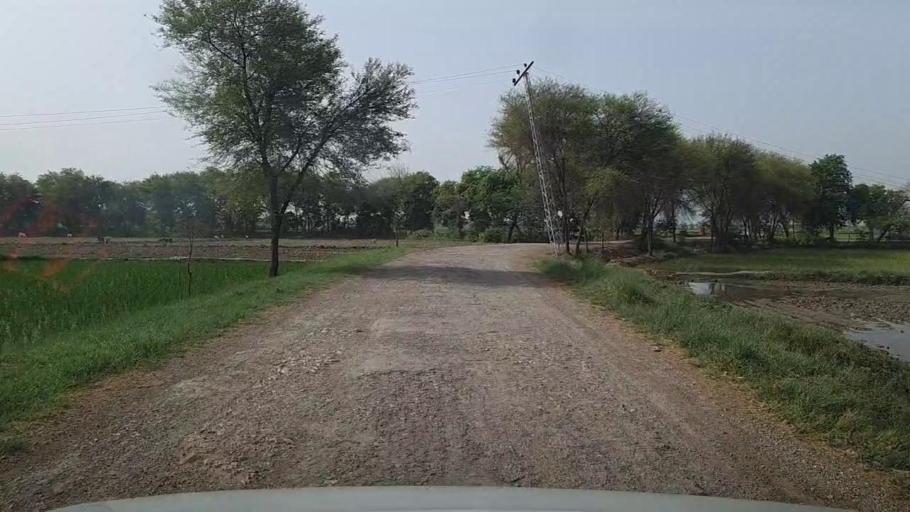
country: PK
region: Sindh
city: Mehar
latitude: 27.1049
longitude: 67.8214
